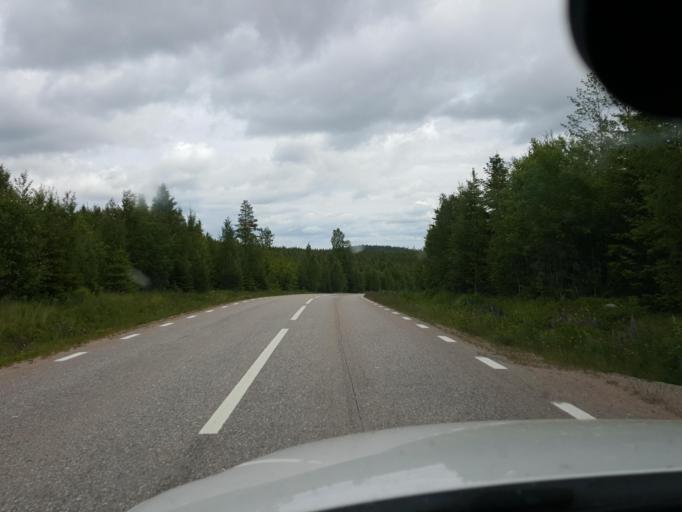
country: SE
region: Gaevleborg
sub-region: Ljusdals Kommun
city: Farila
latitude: 61.7654
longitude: 15.5722
